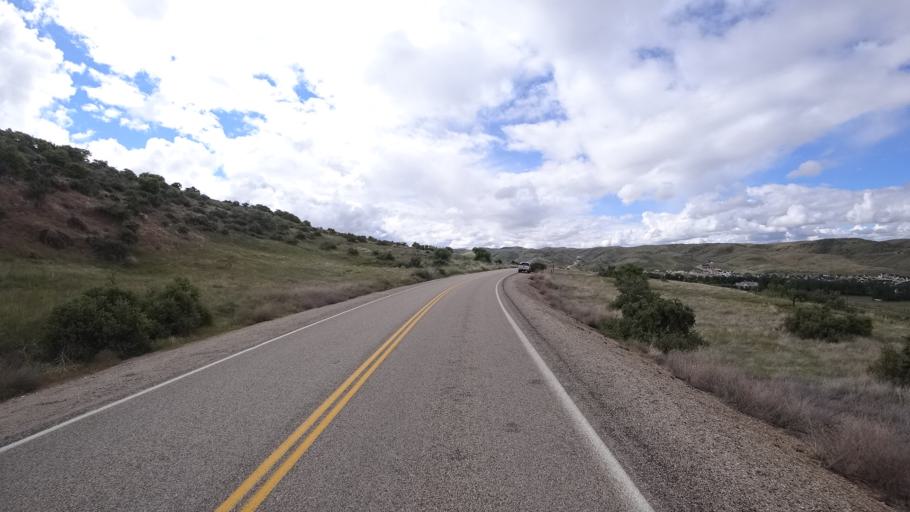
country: US
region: Idaho
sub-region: Ada County
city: Garden City
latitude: 43.7217
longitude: -116.2346
